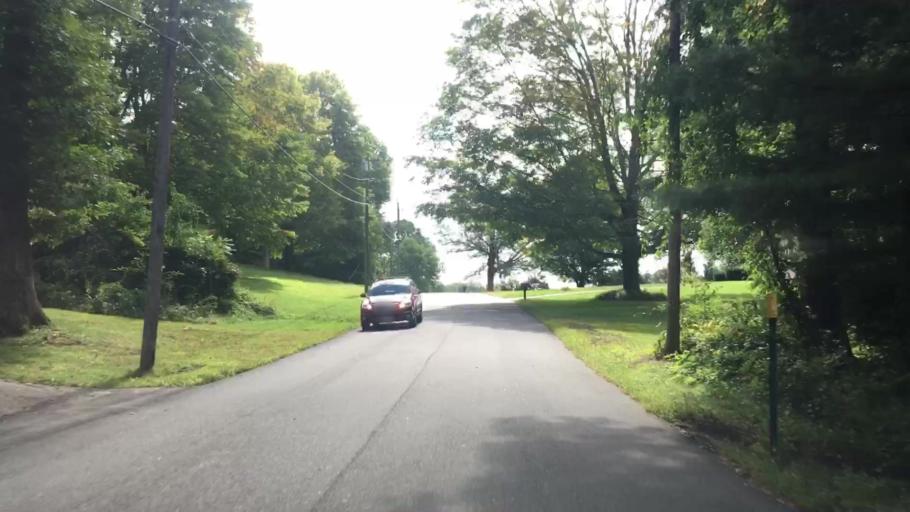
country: US
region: Connecticut
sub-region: Tolland County
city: Stafford Springs
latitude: 41.9247
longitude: -72.2404
